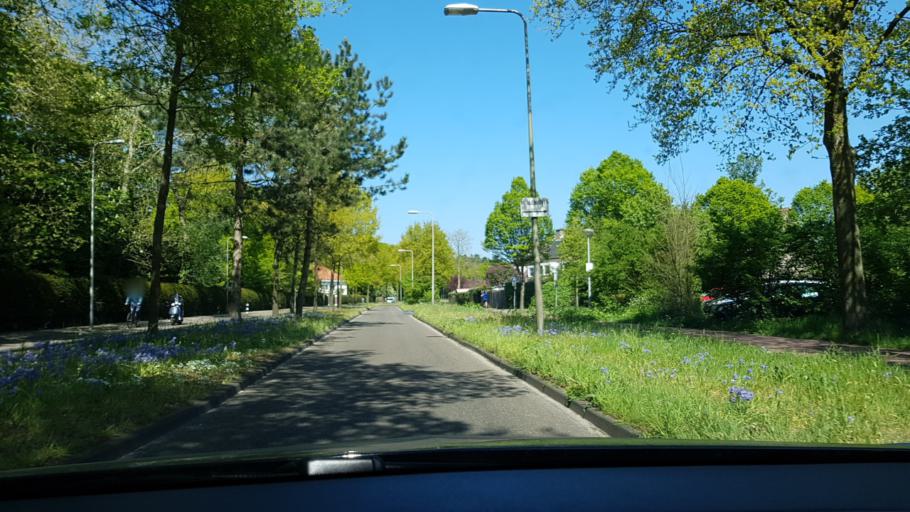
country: NL
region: North Holland
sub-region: Gemeente Heemstede
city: Heemstede
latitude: 52.3341
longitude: 4.6159
